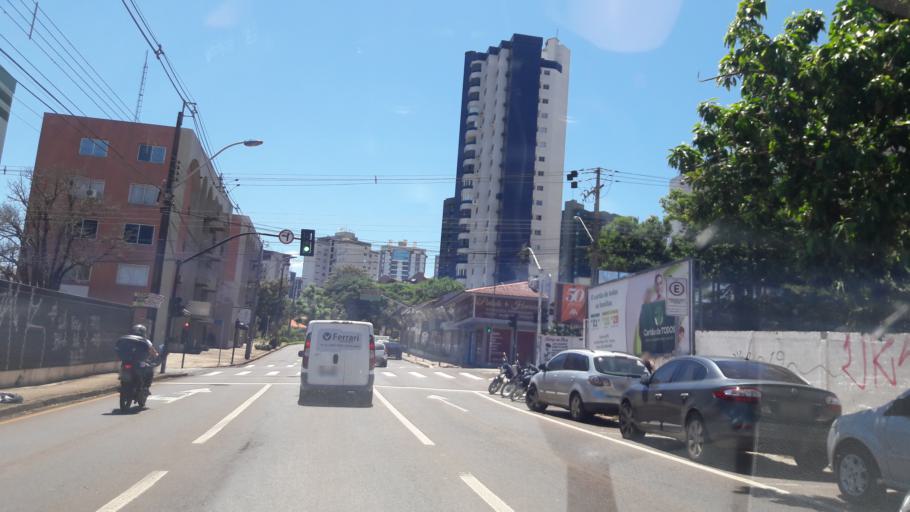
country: BR
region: Parana
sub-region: Cascavel
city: Cascavel
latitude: -24.9523
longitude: -53.4592
